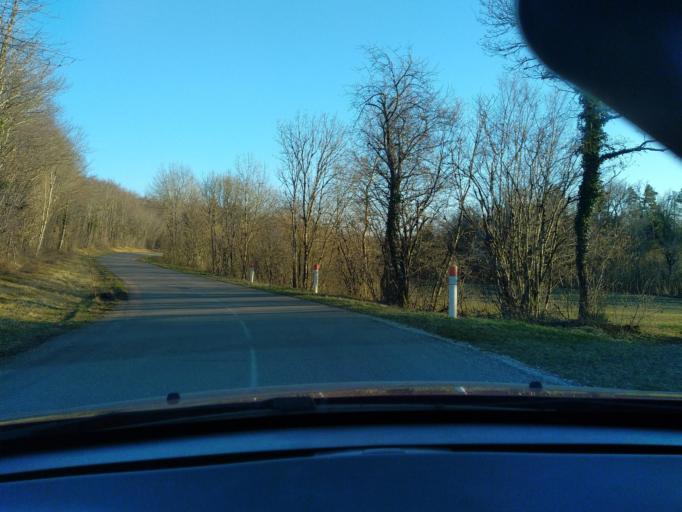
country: FR
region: Franche-Comte
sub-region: Departement du Jura
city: Perrigny
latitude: 46.6173
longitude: 5.6416
